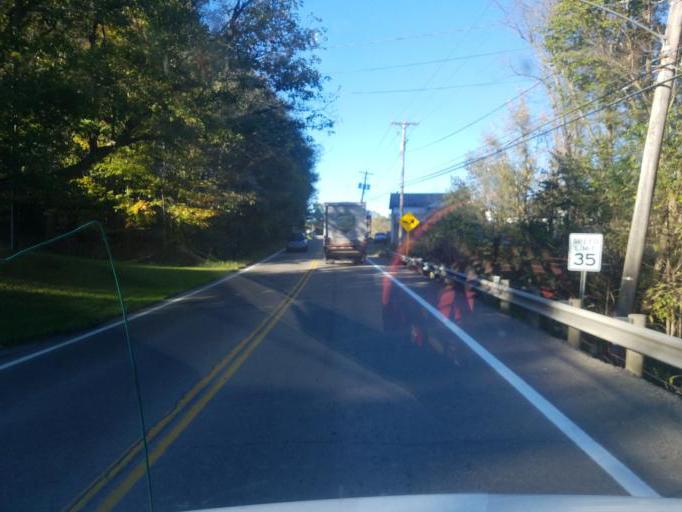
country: US
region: Ohio
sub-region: Columbiana County
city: New Waterford
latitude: 40.7865
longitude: -80.6250
